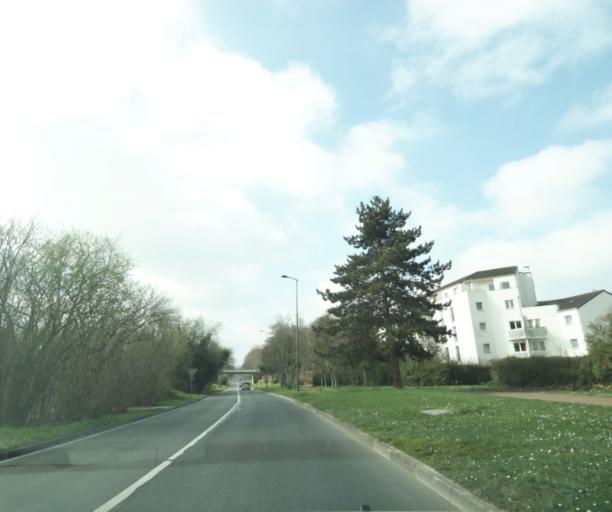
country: FR
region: Ile-de-France
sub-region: Departement du Val-d'Oise
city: Vaureal
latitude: 49.0479
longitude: 2.0437
